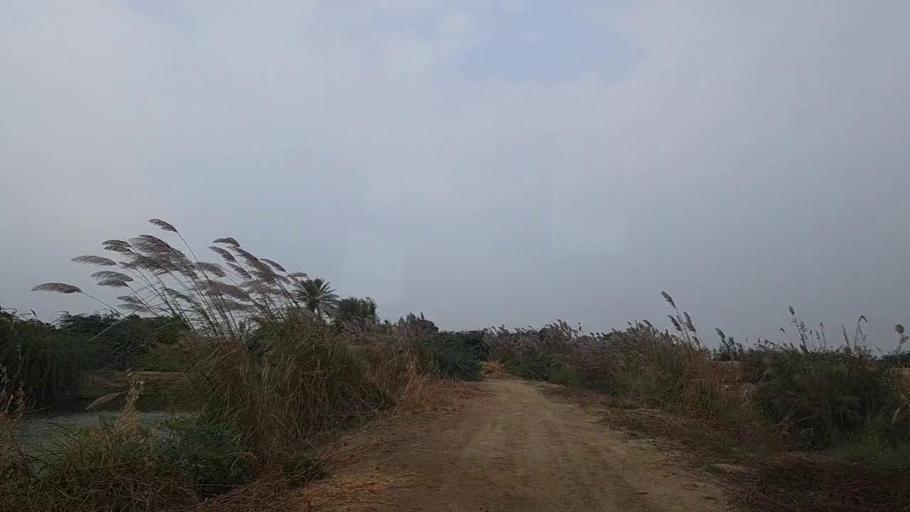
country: PK
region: Sindh
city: Gharo
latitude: 24.6279
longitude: 67.5035
